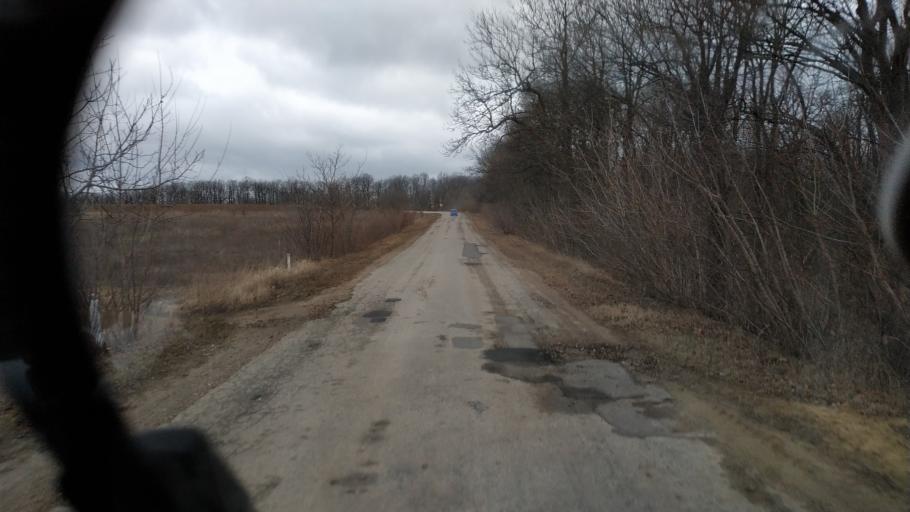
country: MD
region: Calarasi
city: Calarasi
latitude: 47.2261
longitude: 28.2375
